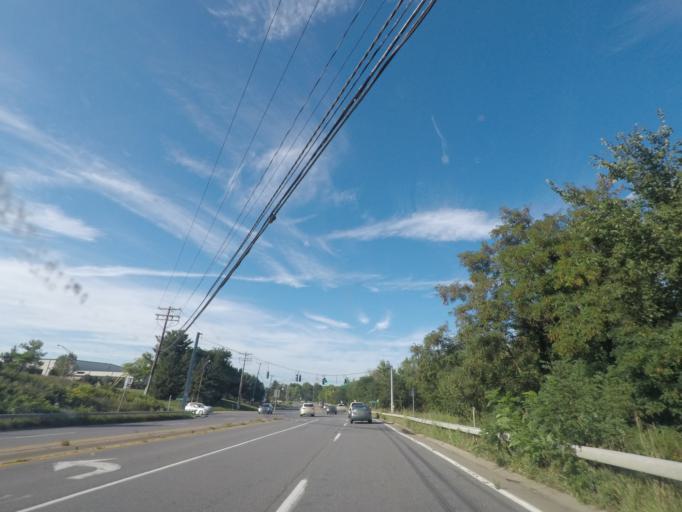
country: US
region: New York
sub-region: Schenectady County
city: Niskayuna
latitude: 42.7579
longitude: -73.8147
